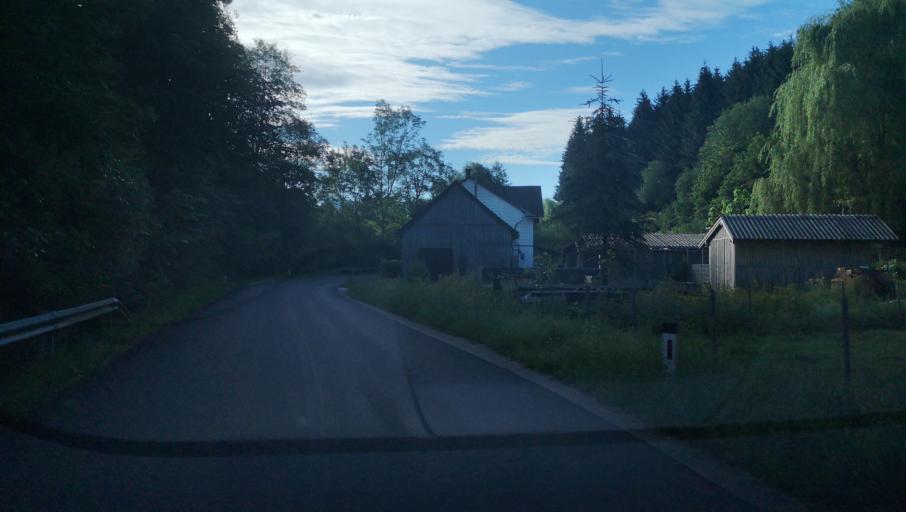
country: AT
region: Lower Austria
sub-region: Politischer Bezirk Scheibbs
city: Gresten
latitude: 48.0065
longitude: 15.0422
